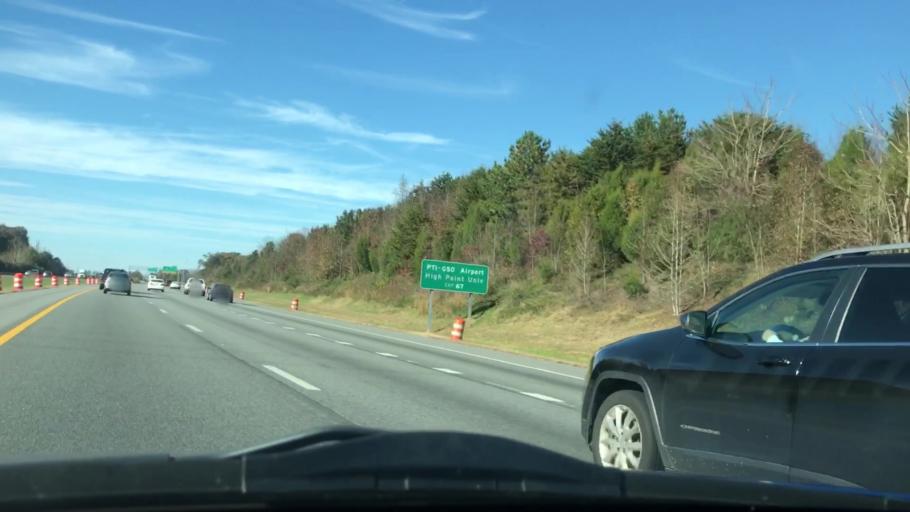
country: US
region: North Carolina
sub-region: Guilford County
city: High Point
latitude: 35.9944
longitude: -79.9861
